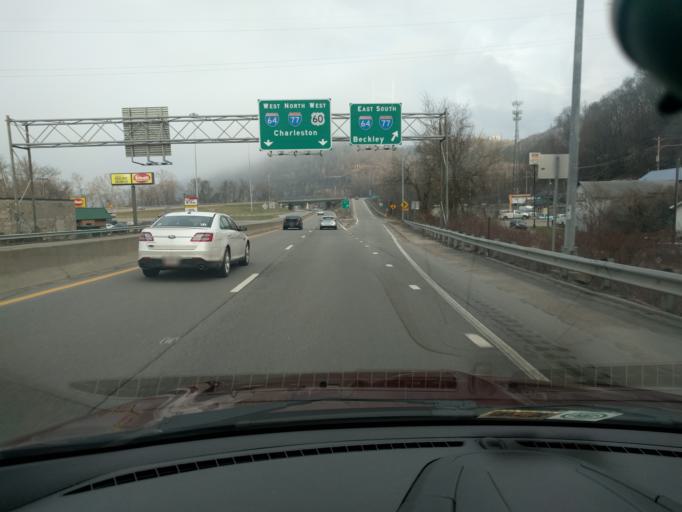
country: US
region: West Virginia
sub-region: Kanawha County
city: Rand
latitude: 38.3128
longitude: -81.5589
